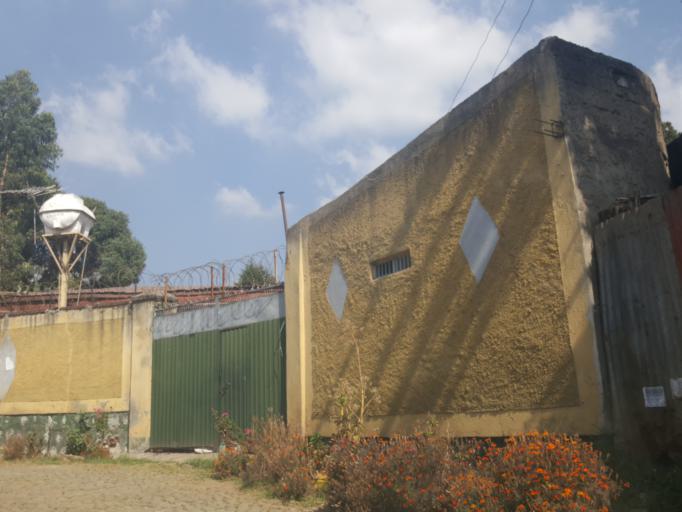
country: ET
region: Adis Abeba
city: Addis Ababa
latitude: 9.0519
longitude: 38.7342
